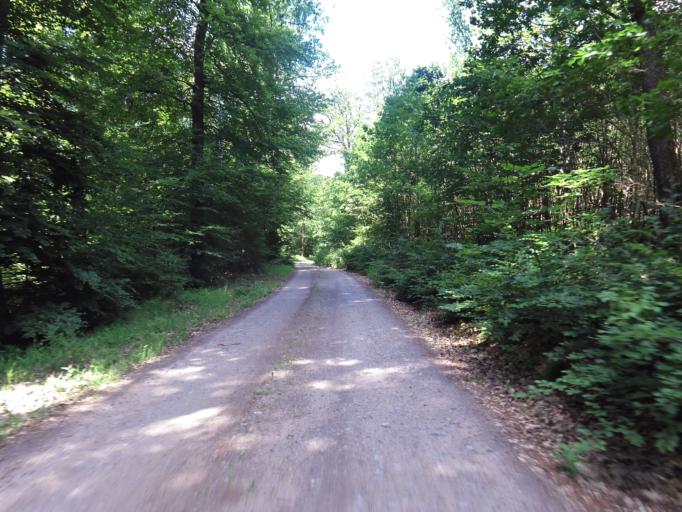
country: DE
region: Rheinland-Pfalz
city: Eusserthal
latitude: 49.2898
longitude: 7.9385
